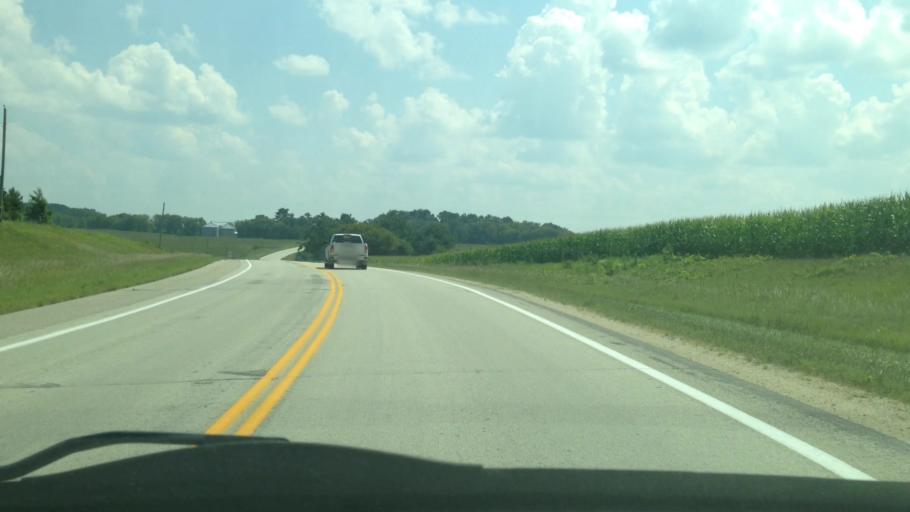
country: US
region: Minnesota
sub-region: Olmsted County
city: Stewartville
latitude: 43.8829
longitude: -92.4085
